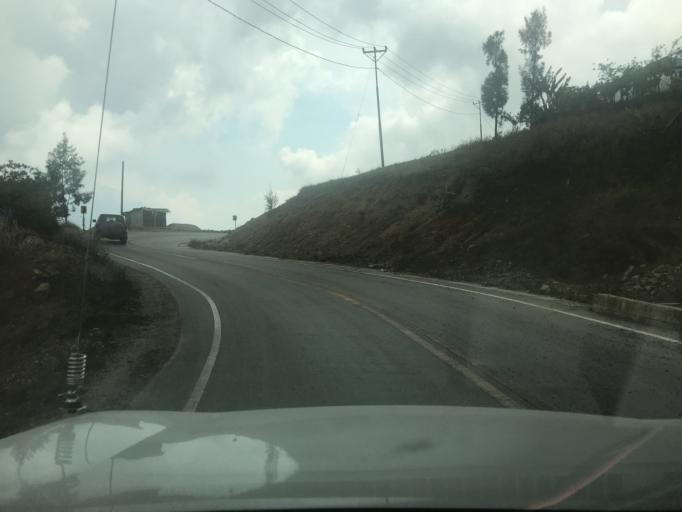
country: TL
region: Manufahi
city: Same
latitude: -8.8902
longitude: 125.5986
